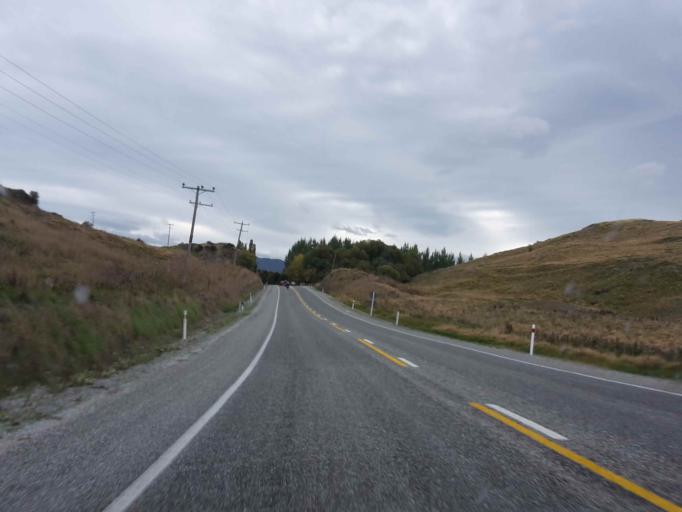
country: NZ
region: Otago
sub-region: Queenstown-Lakes District
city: Arrowtown
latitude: -44.9791
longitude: 168.8321
